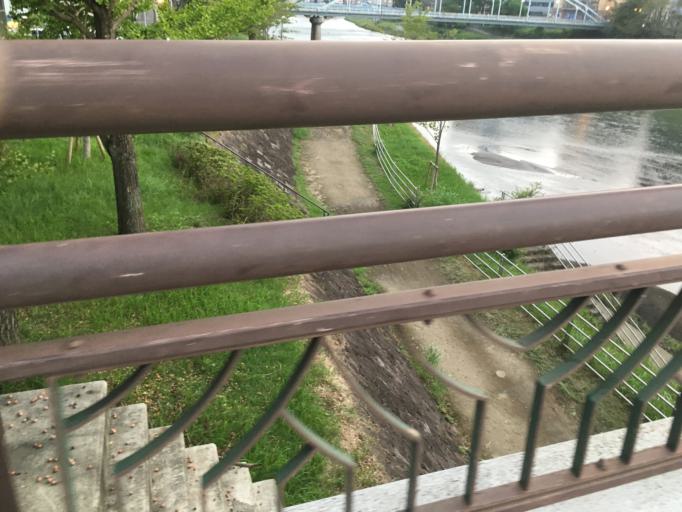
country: JP
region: Kumamoto
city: Kumamoto
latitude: 32.8013
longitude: 130.7152
